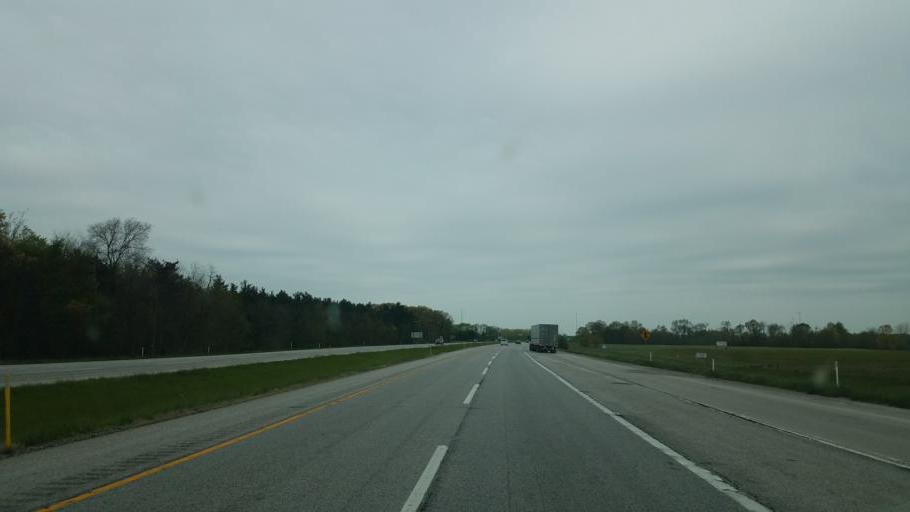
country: US
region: Michigan
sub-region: Saint Joseph County
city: White Pigeon
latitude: 41.7483
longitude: -85.6692
